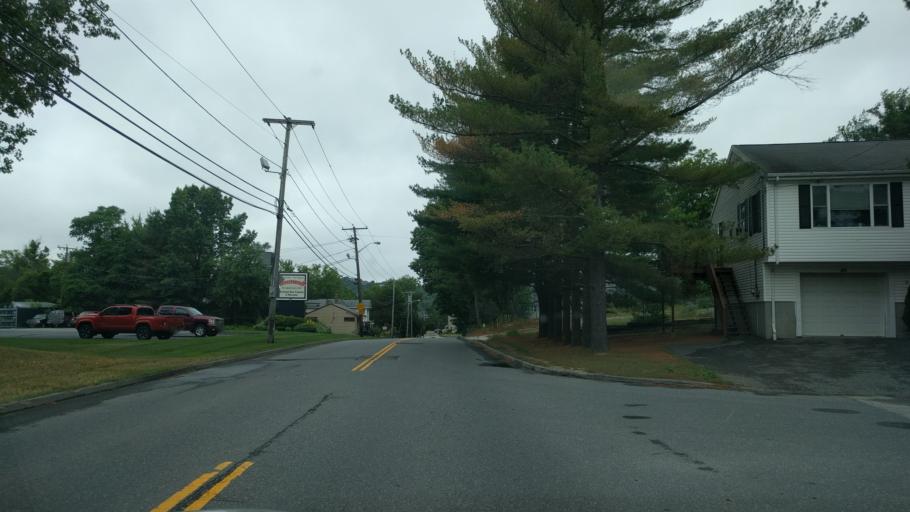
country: US
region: Massachusetts
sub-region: Worcester County
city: Sunderland
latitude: 42.2473
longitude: -71.7689
